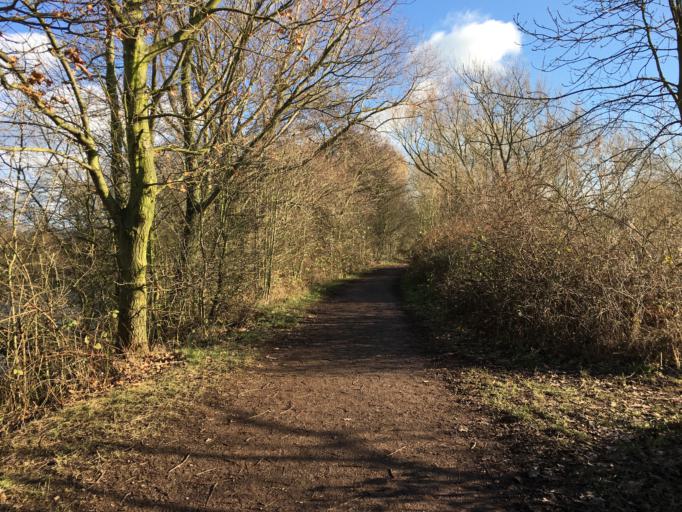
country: GB
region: England
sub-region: Nottinghamshire
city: Gotham
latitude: 52.9071
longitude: -1.2160
